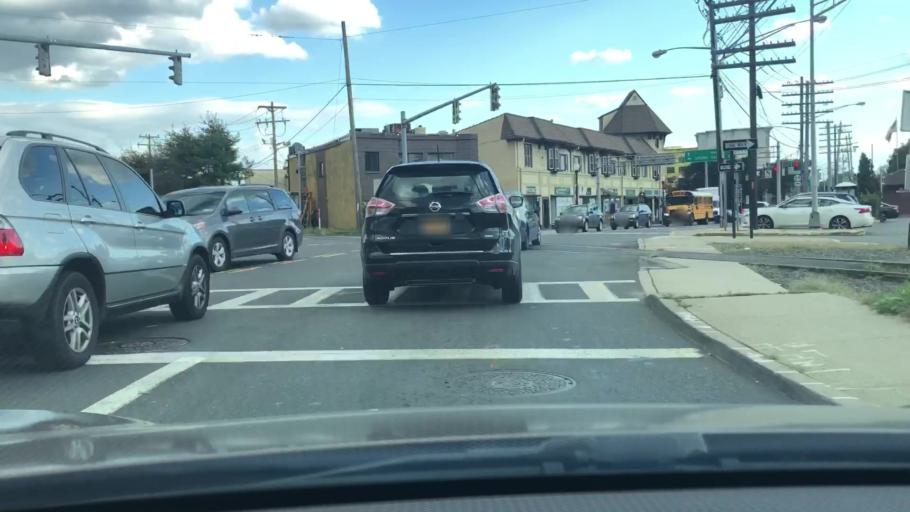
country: US
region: New York
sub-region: Rockland County
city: Suffern
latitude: 41.1172
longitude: -74.1552
